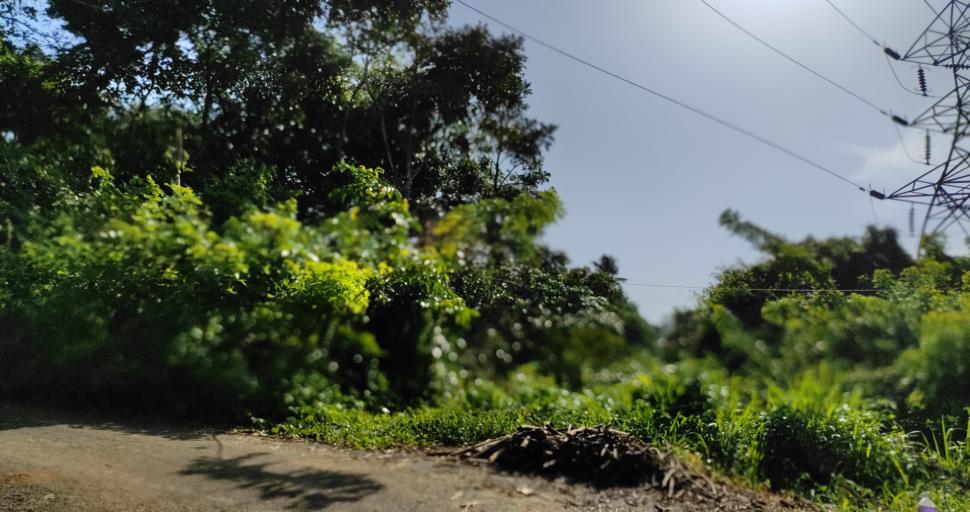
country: IN
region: Kerala
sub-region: Alappuzha
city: Shertallai
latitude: 9.6090
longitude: 76.3345
